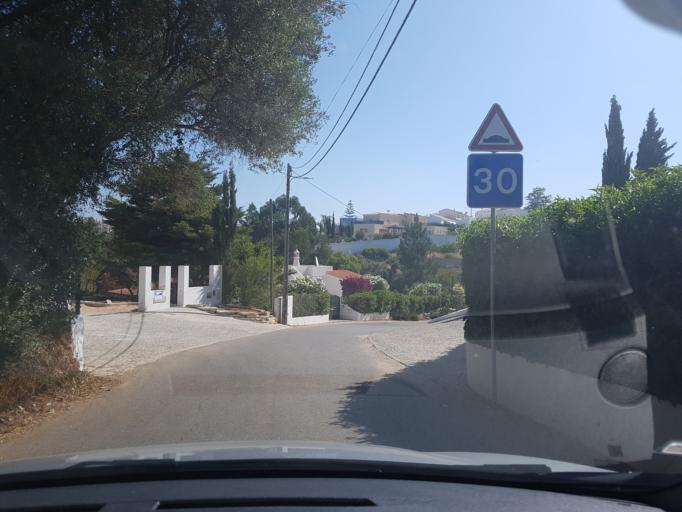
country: PT
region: Faro
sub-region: Lagoa
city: Carvoeiro
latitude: 37.0989
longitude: -8.4620
